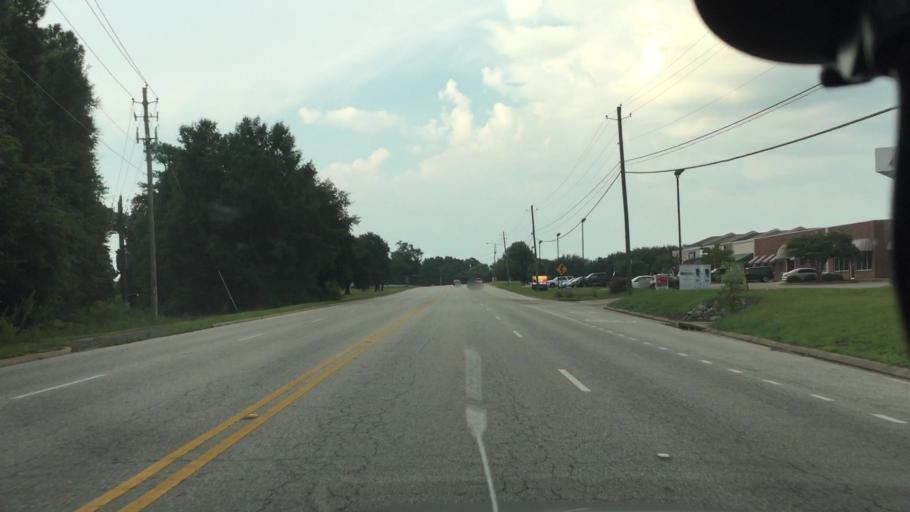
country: US
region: Alabama
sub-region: Coffee County
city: Enterprise
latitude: 31.3463
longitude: -85.8372
